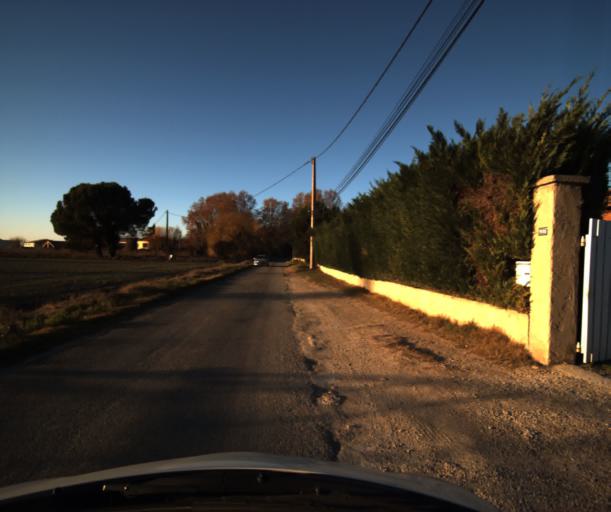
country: FR
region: Provence-Alpes-Cote d'Azur
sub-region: Departement du Vaucluse
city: Pertuis
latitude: 43.6807
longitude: 5.5095
